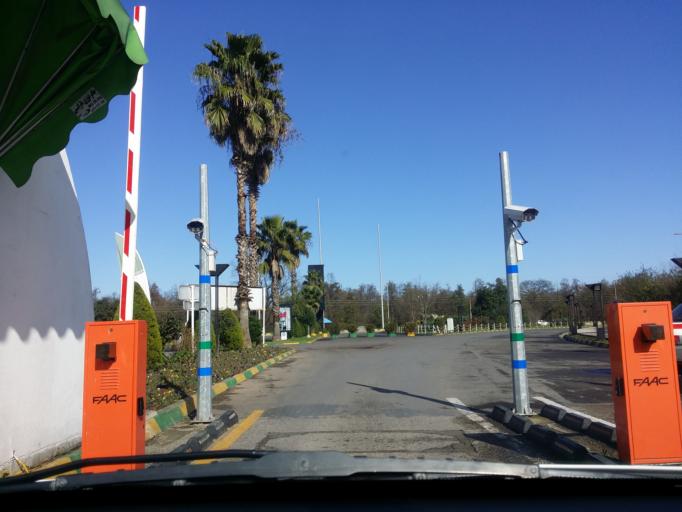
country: IR
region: Mazandaran
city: Chalus
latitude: 36.6865
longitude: 51.3060
